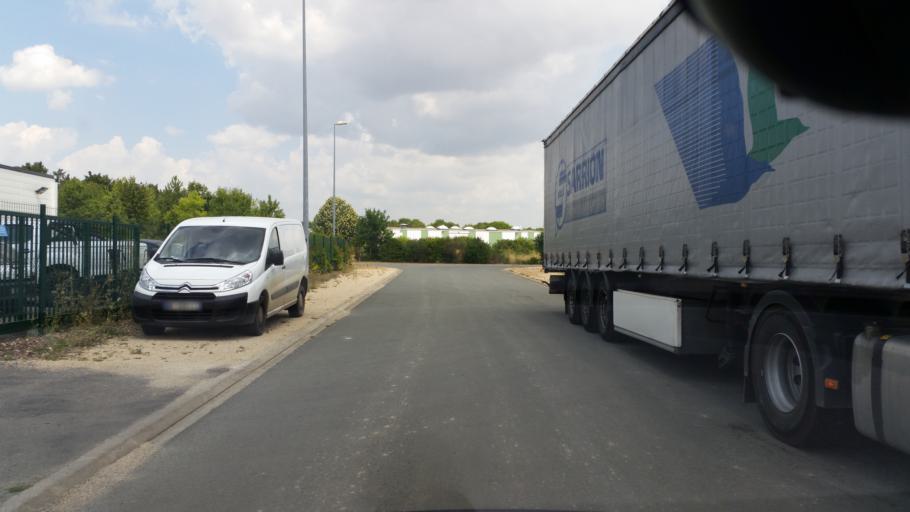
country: FR
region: Poitou-Charentes
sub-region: Departement de la Charente-Maritime
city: Surgeres
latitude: 46.1059
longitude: -0.7721
